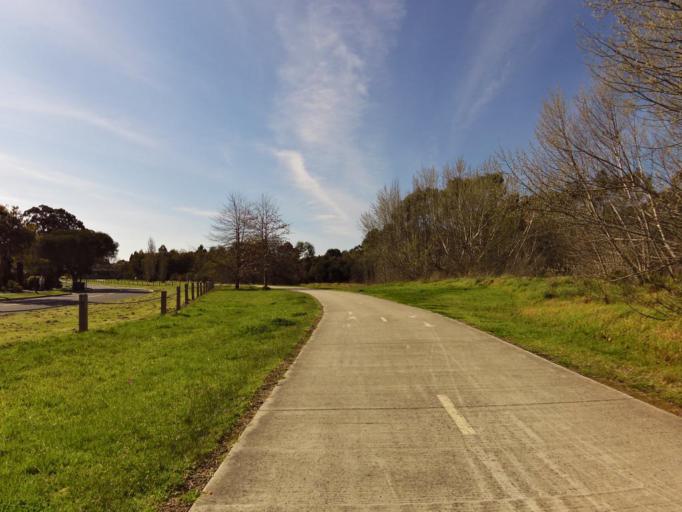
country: AU
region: Victoria
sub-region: Monash
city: Mulgrave
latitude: -37.9143
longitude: 145.2028
